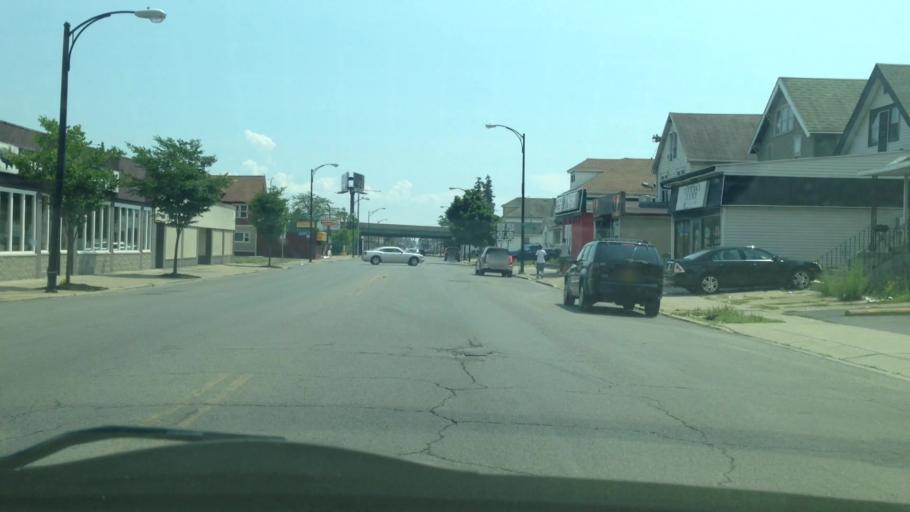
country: US
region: New York
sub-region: Erie County
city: Eggertsville
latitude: 42.9346
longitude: -78.8137
